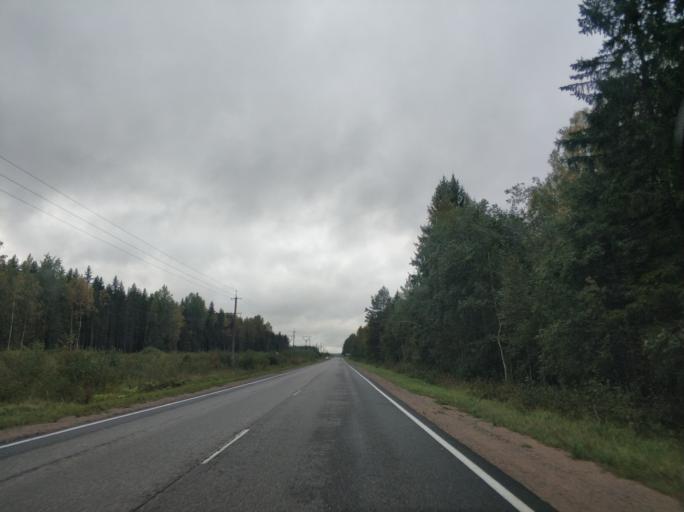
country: RU
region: Leningrad
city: Borisova Griva
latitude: 60.1026
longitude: 30.9569
